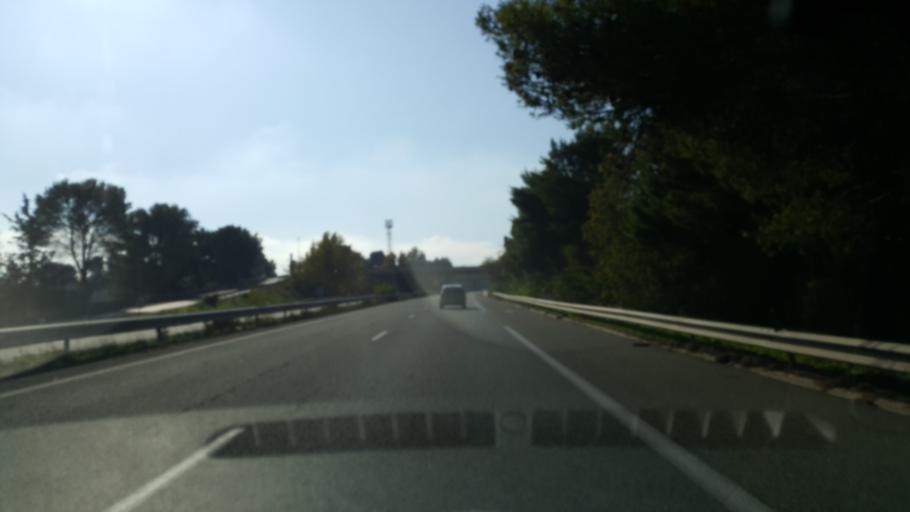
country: FR
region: Provence-Alpes-Cote d'Azur
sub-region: Departement des Bouches-du-Rhone
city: Aubagne
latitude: 43.3059
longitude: 5.5745
